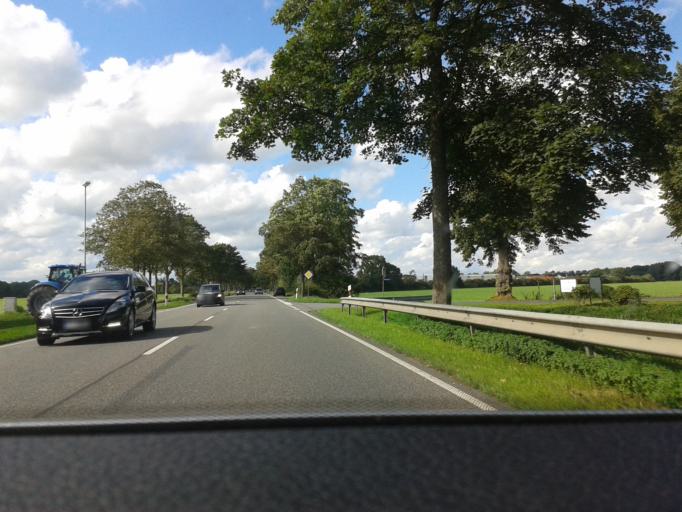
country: DE
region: North Rhine-Westphalia
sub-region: Regierungsbezirk Dusseldorf
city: Weeze
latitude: 51.6137
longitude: 6.2191
